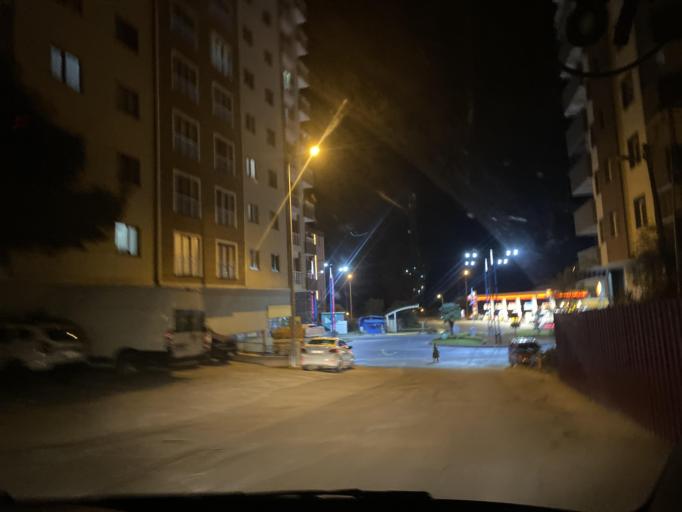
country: TR
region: Trabzon
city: Yomra
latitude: 40.9573
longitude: 39.8520
